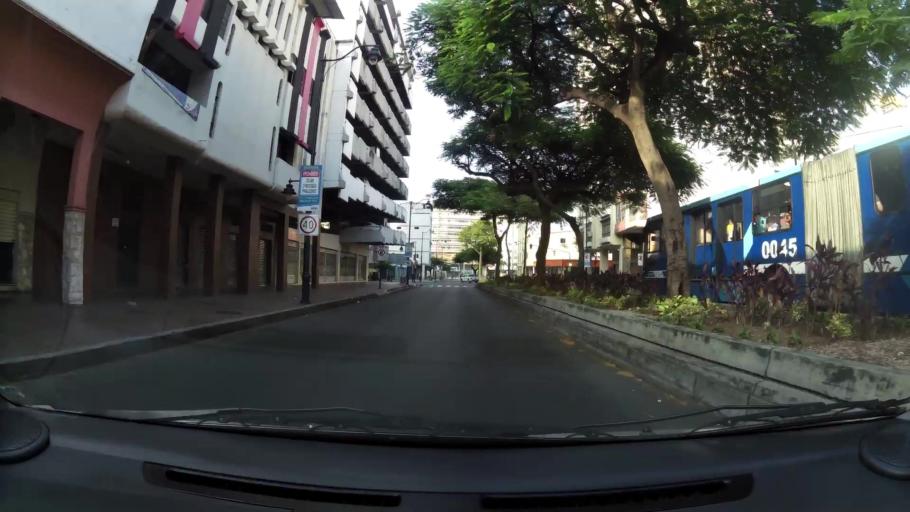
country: EC
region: Guayas
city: Guayaquil
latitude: -2.1958
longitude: -79.8850
